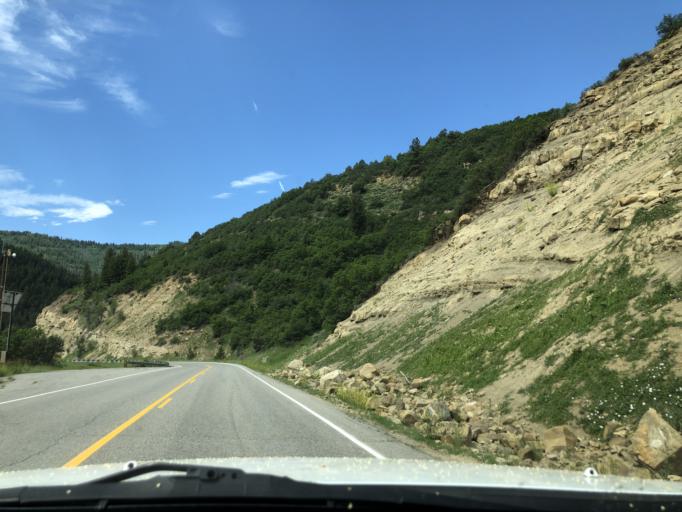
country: US
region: Colorado
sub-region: Delta County
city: Paonia
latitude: 38.9467
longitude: -107.3483
